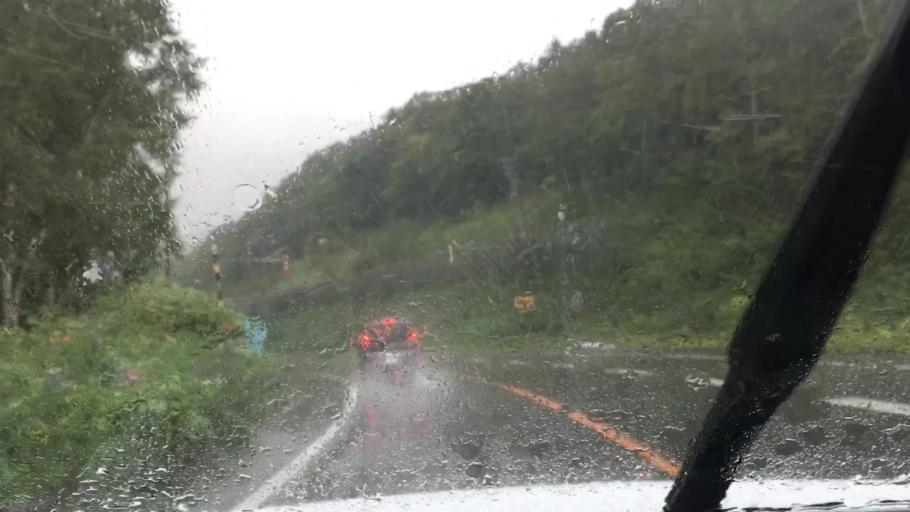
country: JP
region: Hokkaido
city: Sapporo
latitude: 42.8489
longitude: 141.0801
